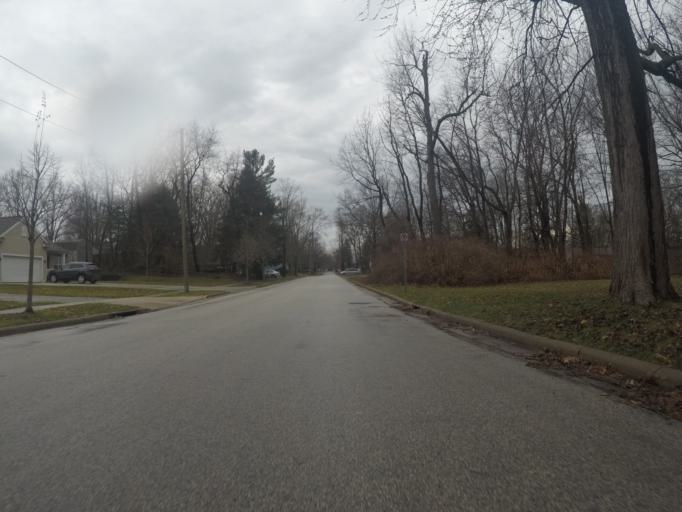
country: US
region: Ohio
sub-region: Portage County
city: Kent
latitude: 41.1430
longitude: -81.3549
